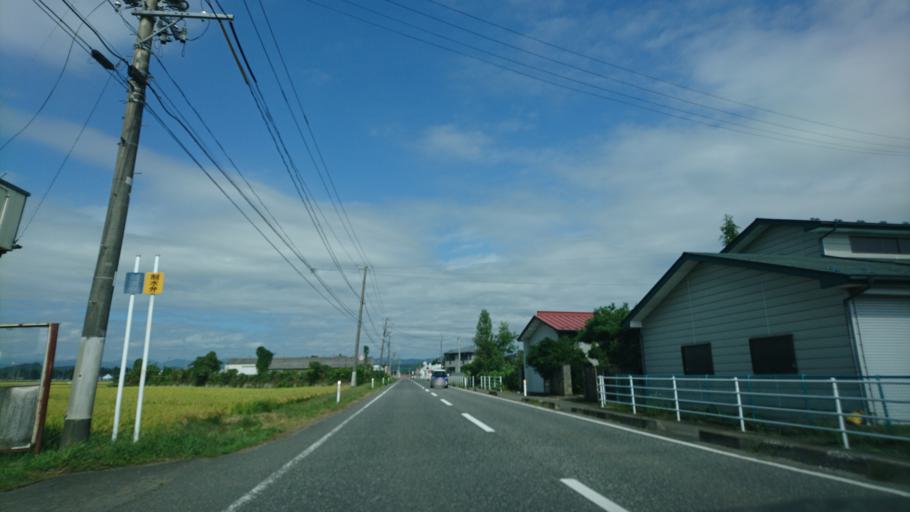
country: JP
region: Miyagi
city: Furukawa
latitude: 38.7369
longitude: 140.9514
